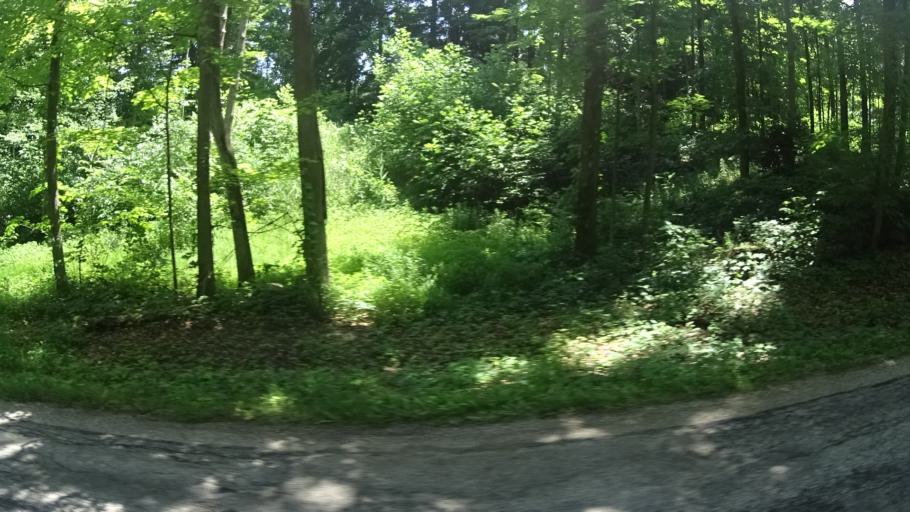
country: US
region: Ohio
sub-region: Lorain County
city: Vermilion
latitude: 41.3513
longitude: -82.3976
